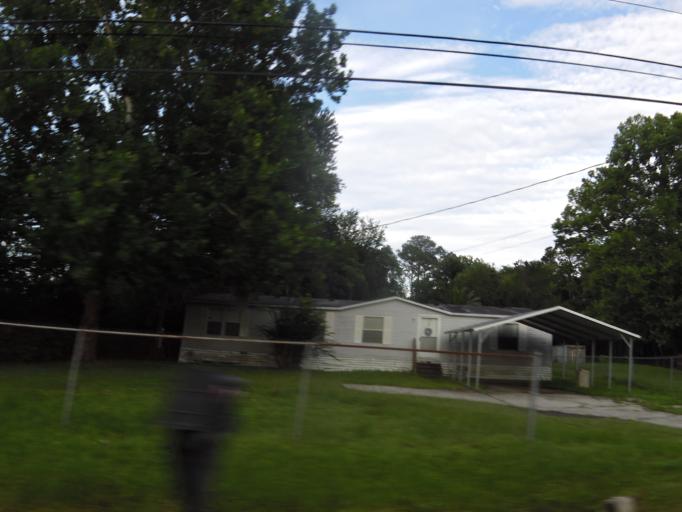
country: US
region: Florida
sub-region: Duval County
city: Jacksonville
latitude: 30.3282
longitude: -81.8066
